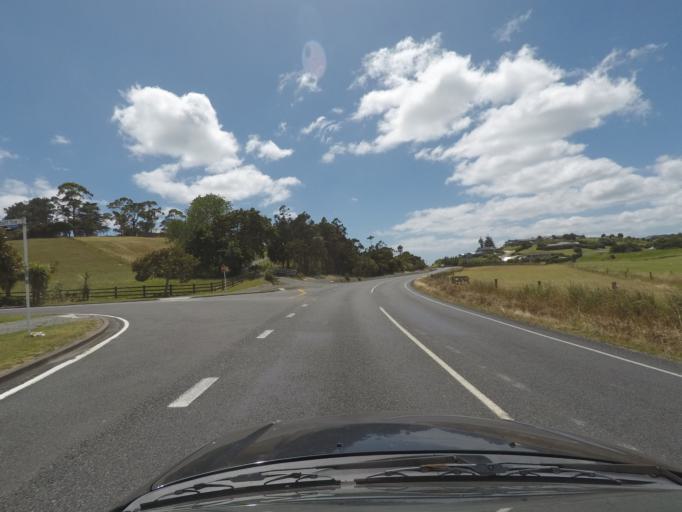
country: NZ
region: Northland
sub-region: Whangarei
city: Ruakaka
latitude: -35.9934
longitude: 174.4651
